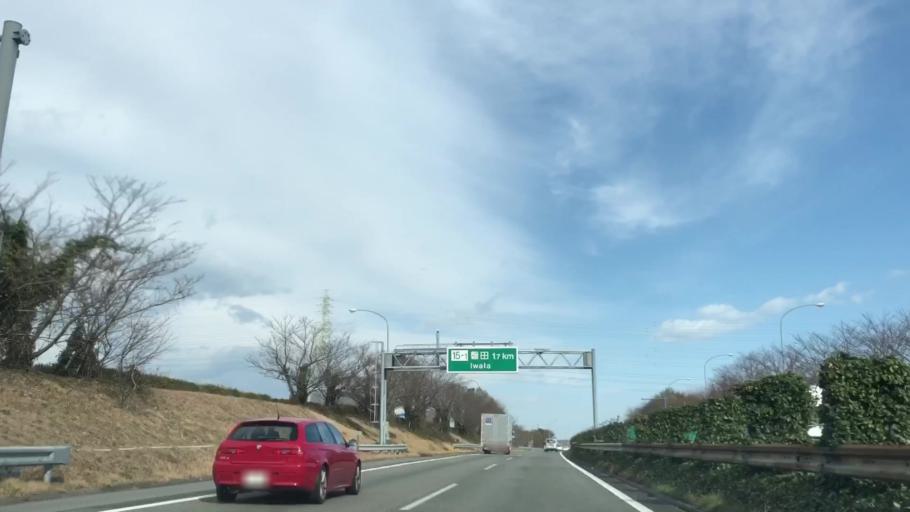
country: JP
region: Shizuoka
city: Iwata
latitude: 34.7482
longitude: 137.8389
